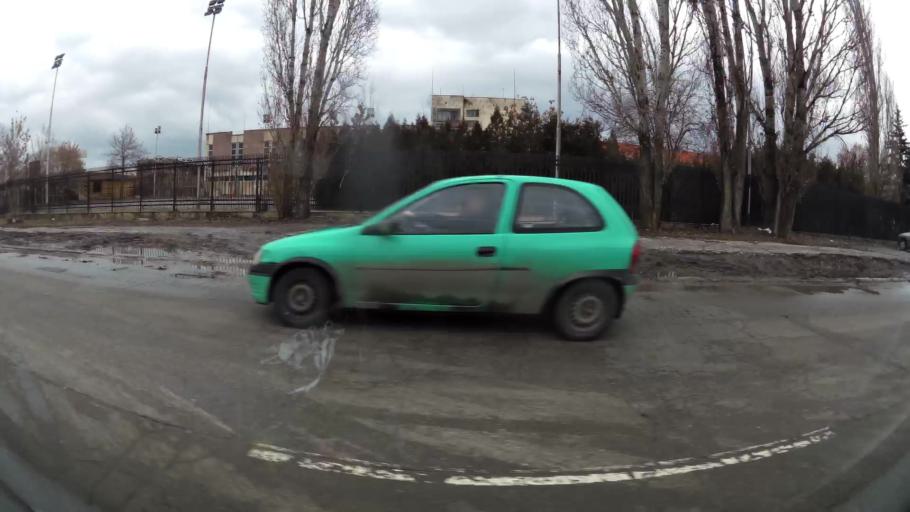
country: BG
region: Sofia-Capital
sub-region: Stolichna Obshtina
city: Sofia
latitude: 42.7200
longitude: 23.2800
